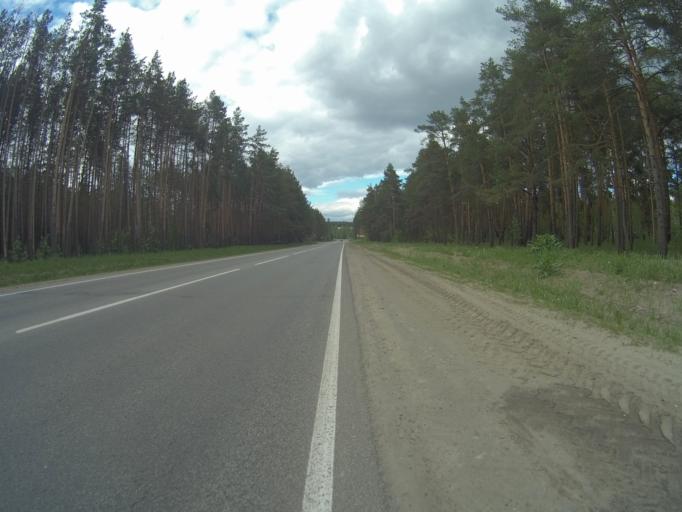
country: RU
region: Vladimir
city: Kommunar
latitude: 56.0442
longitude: 40.4336
